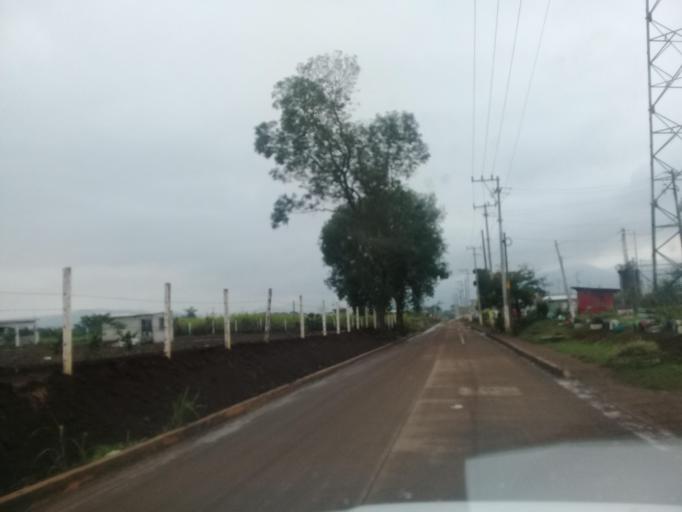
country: MX
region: Veracruz
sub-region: Cordoba
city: San Jose de Tapia
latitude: 18.8534
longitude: -96.9580
